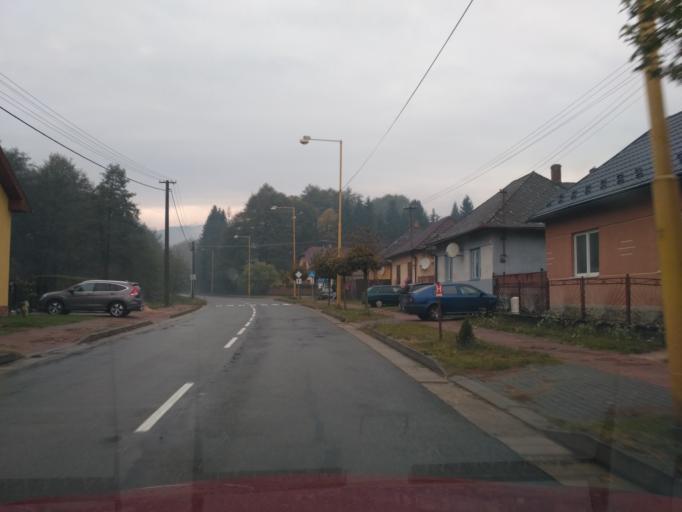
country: SK
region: Kosicky
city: Medzev
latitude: 48.7070
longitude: 20.8823
